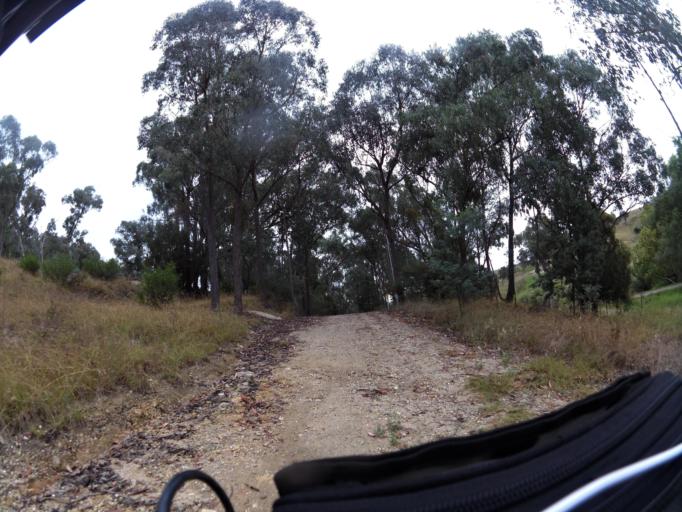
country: AU
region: New South Wales
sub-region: Greater Hume Shire
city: Holbrook
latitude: -36.1555
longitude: 147.4121
